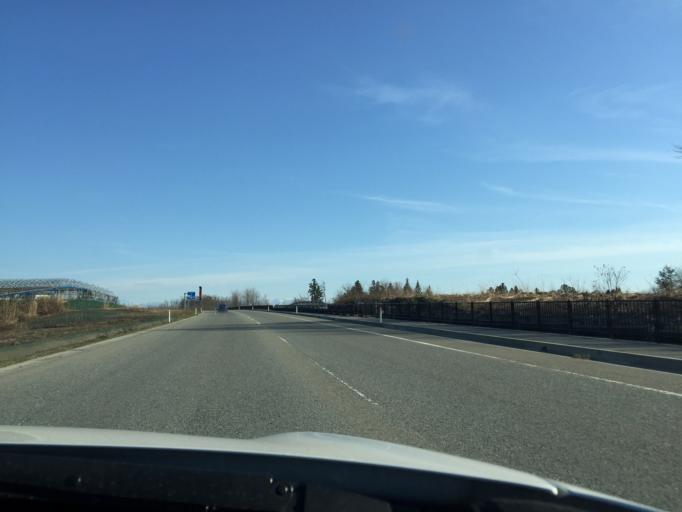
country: JP
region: Yamagata
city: Nagai
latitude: 38.0635
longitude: 140.0526
